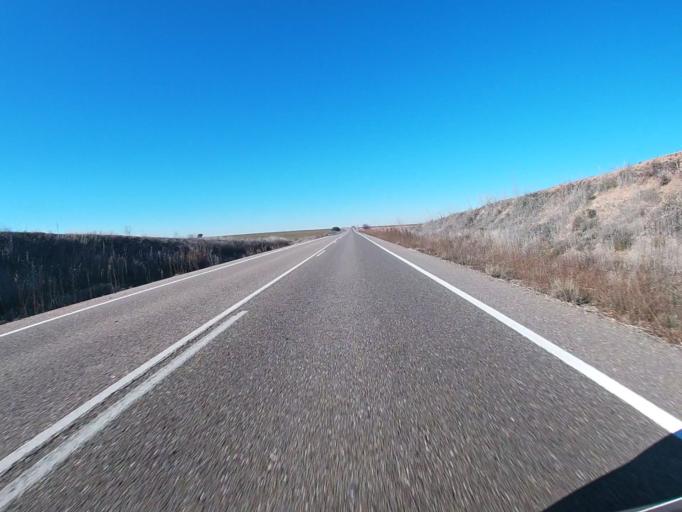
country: ES
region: Castille and Leon
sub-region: Provincia de Salamanca
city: Almenara de Tormes
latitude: 41.0722
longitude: -5.8315
